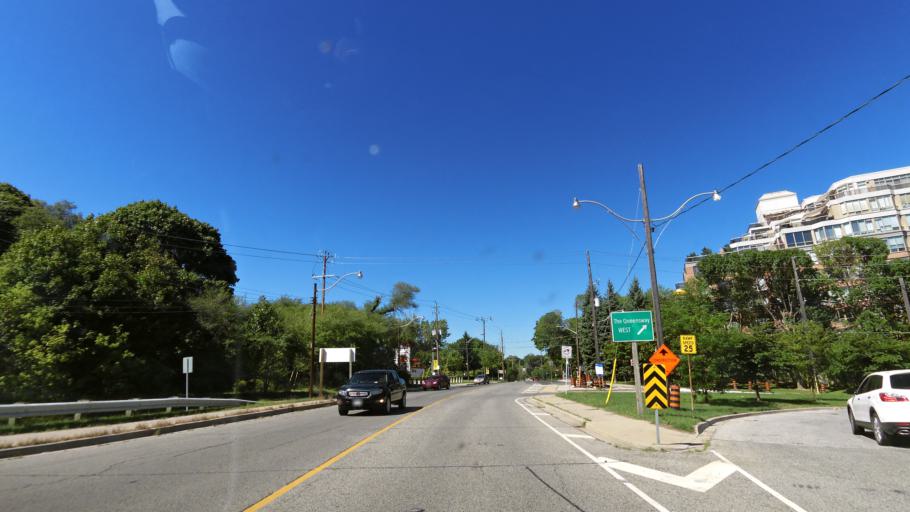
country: CA
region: Ontario
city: Toronto
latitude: 43.6357
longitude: -79.4739
